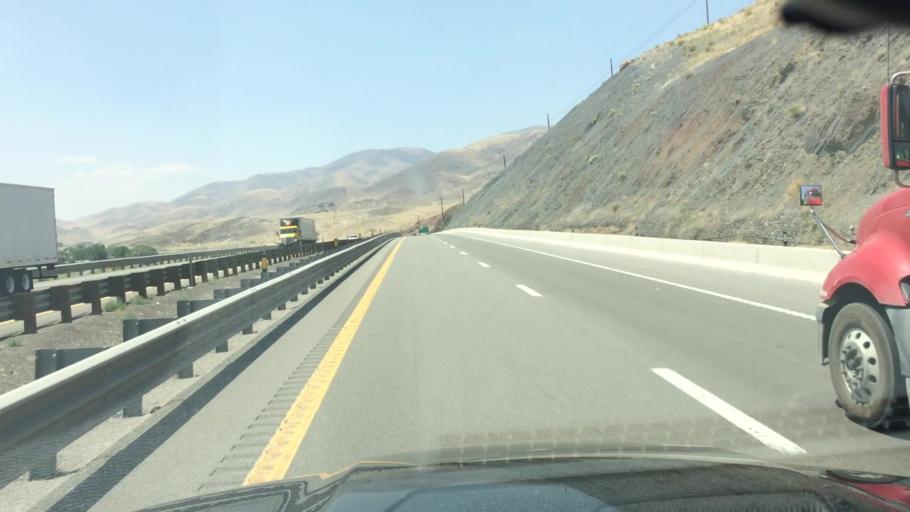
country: US
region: Nevada
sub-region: Lyon County
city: Fernley
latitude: 39.5902
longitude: -119.4026
